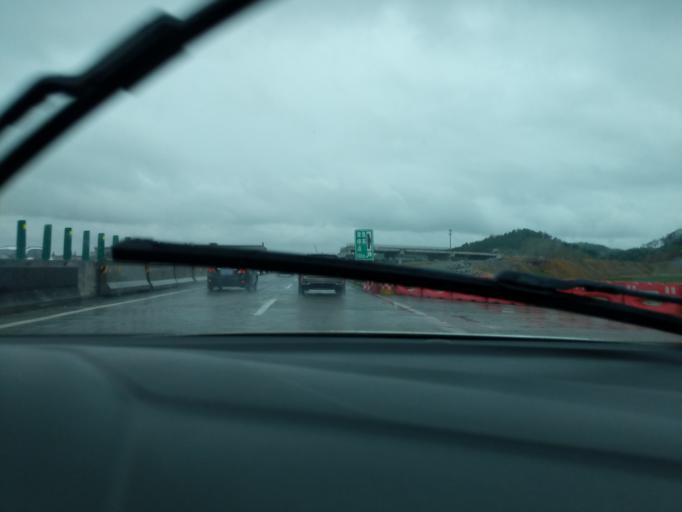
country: CN
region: Guangdong
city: Yueshan
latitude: 22.4642
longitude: 112.7081
